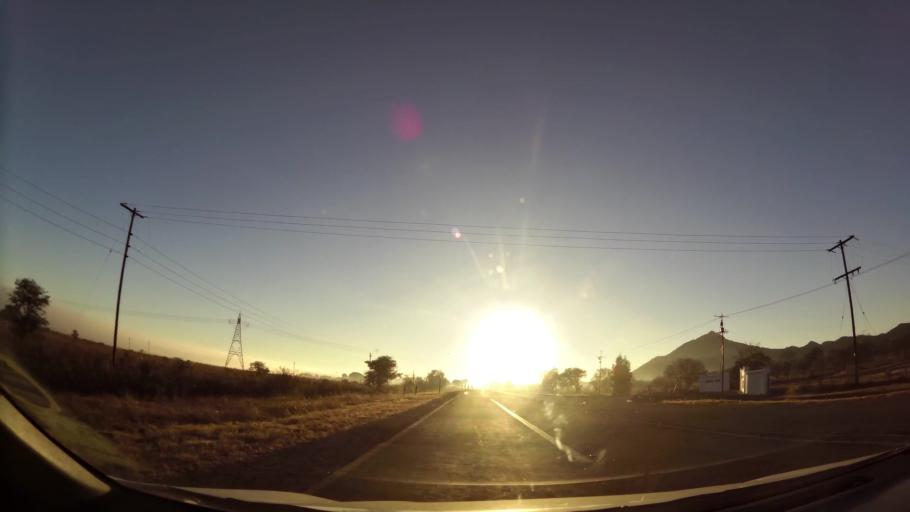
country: ZA
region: Limpopo
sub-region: Capricorn District Municipality
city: Polokwane
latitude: -24.0283
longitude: 29.2931
